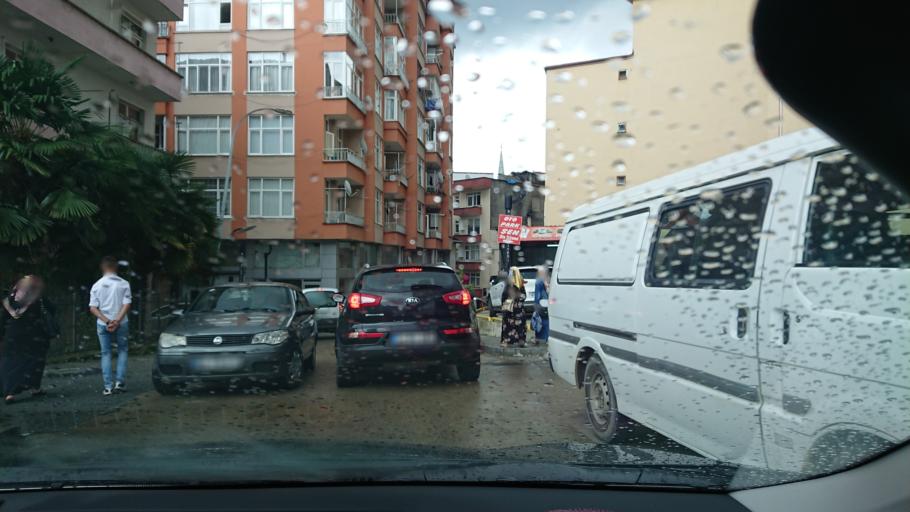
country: TR
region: Rize
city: Rize
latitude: 41.0237
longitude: 40.5176
